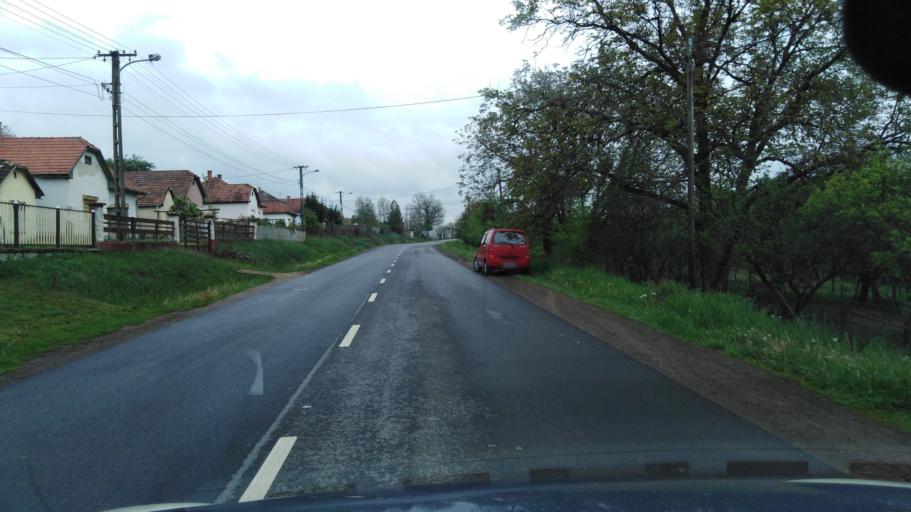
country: HU
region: Nograd
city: Karancskeszi
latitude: 48.1213
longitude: 19.6409
